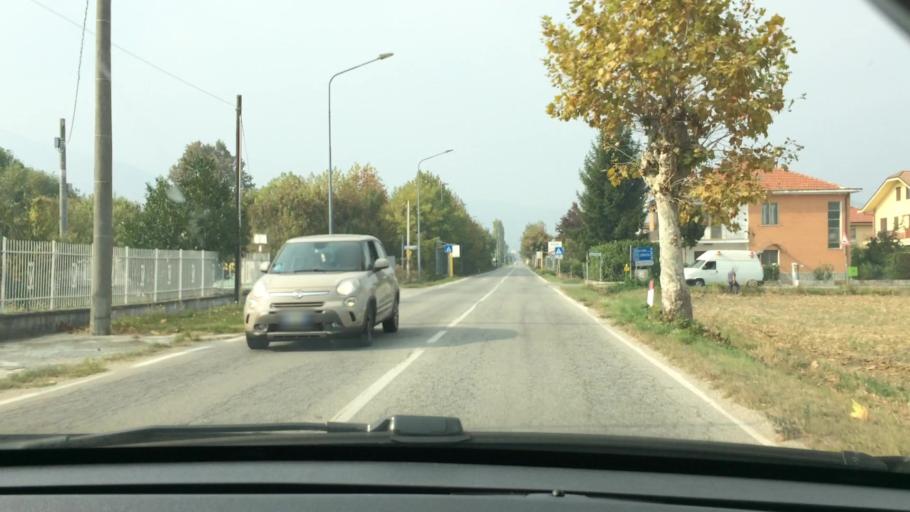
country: IT
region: Piedmont
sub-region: Provincia di Torino
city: Cumiana
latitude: 44.9592
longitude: 7.4043
